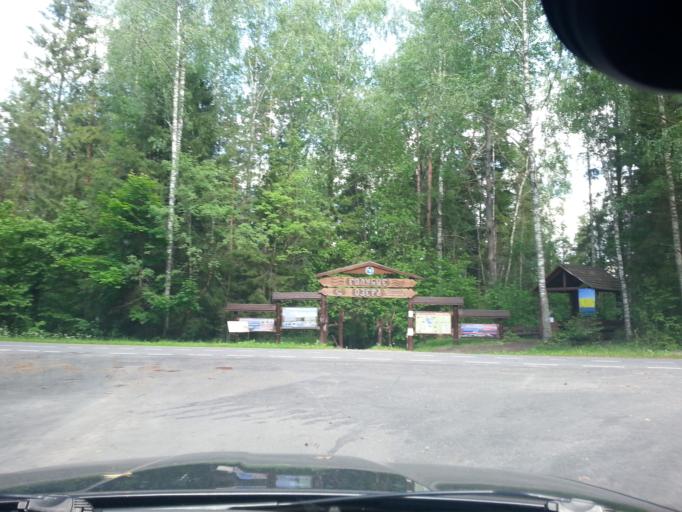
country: BY
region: Vitebsk
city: Lyntupy
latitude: 54.9602
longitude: 26.3612
